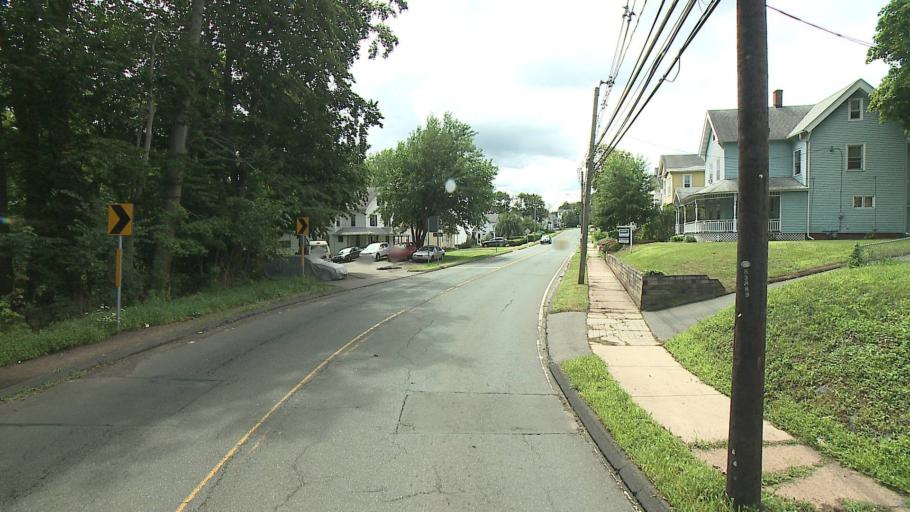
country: US
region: Connecticut
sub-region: Hartford County
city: New Britain
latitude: 41.6521
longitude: -72.7850
